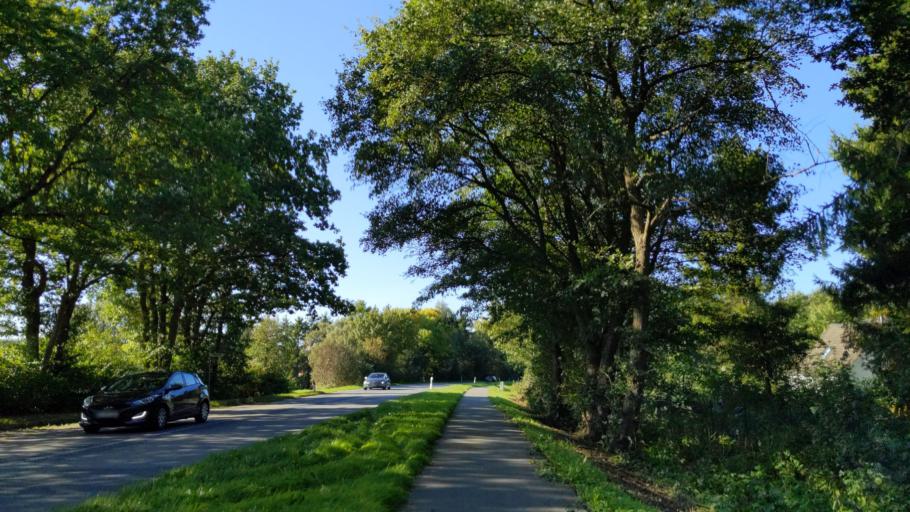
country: DE
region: Schleswig-Holstein
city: Ahrensbok
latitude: 53.9749
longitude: 10.5902
